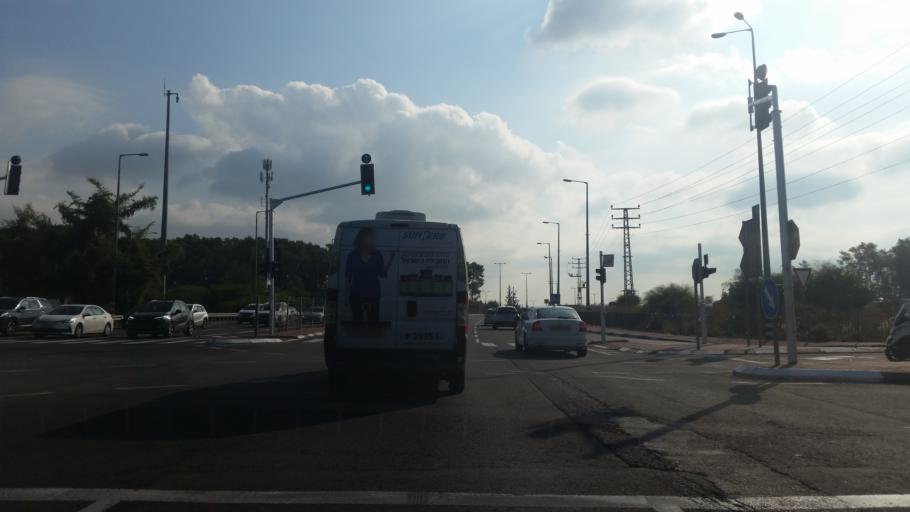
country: PS
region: West Bank
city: Budrus
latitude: 31.9519
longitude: 34.9554
